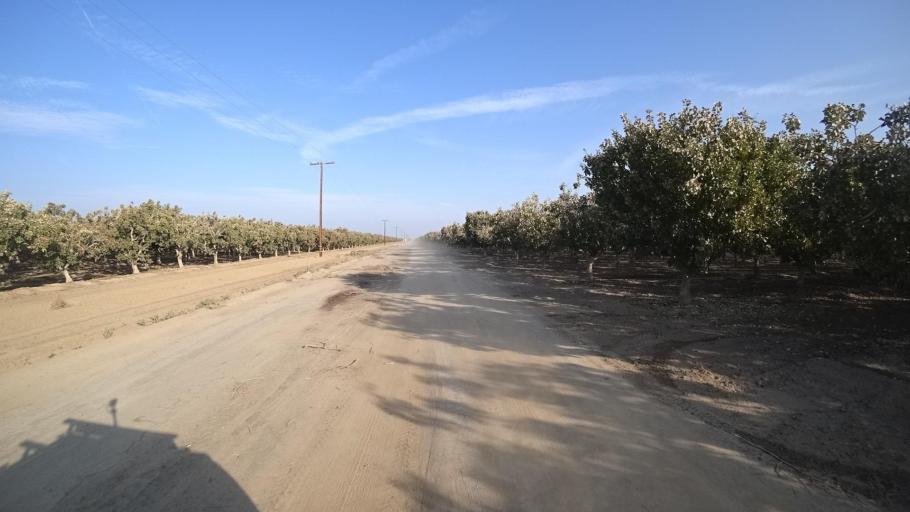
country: US
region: California
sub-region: Kern County
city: McFarland
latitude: 35.7204
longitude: -119.1872
